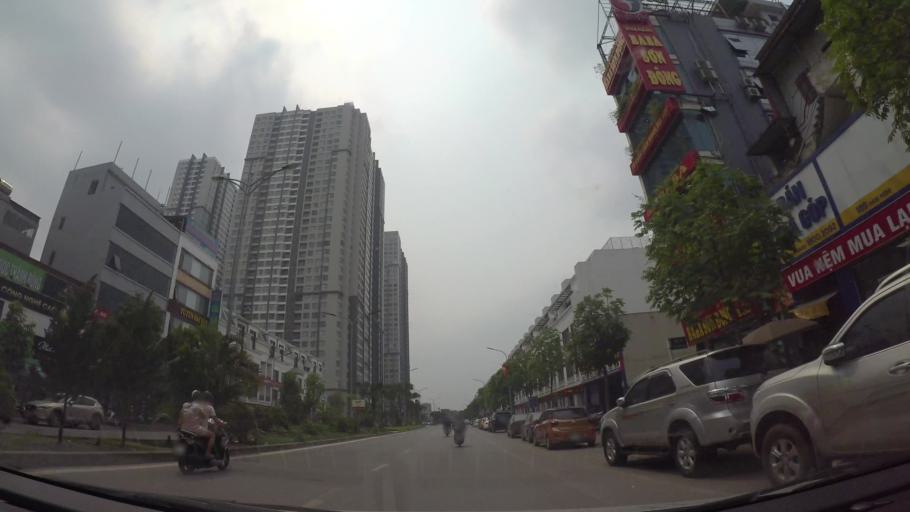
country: VN
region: Ha Noi
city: Cau Dien
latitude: 21.0355
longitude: 105.7630
